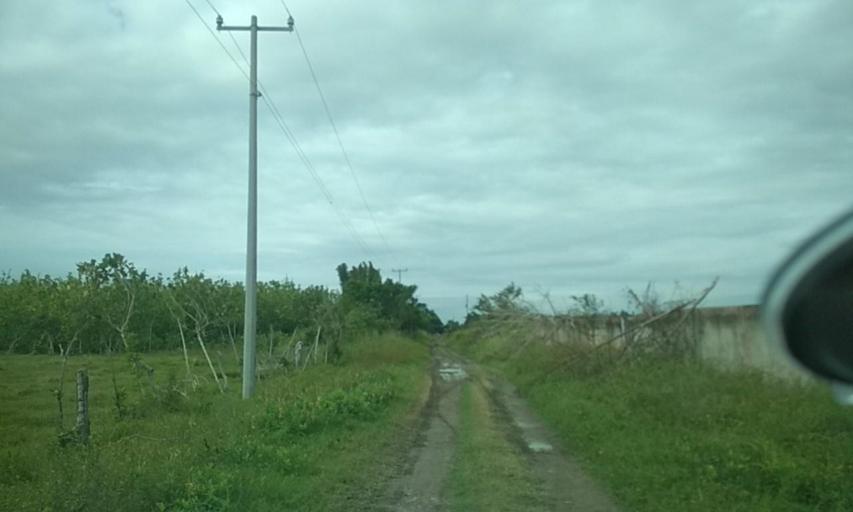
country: MX
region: Veracruz
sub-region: Cazones de Herrera
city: Rancho Nuevo
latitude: 20.6025
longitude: -97.1436
